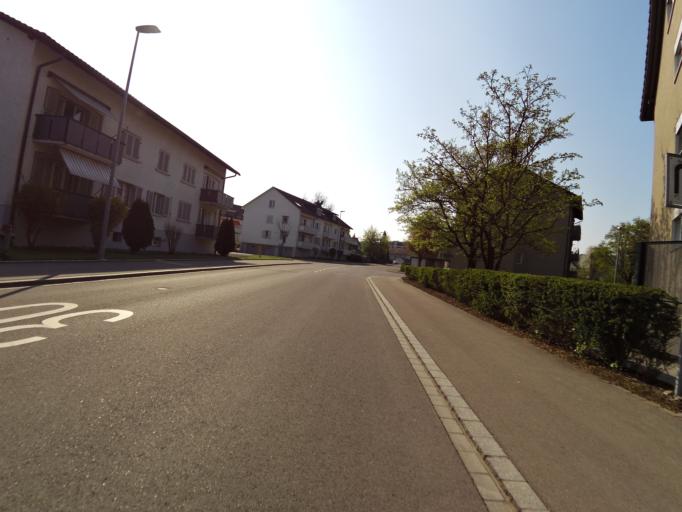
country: CH
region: Thurgau
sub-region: Frauenfeld District
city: Frauenfeld
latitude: 47.5585
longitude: 8.8869
